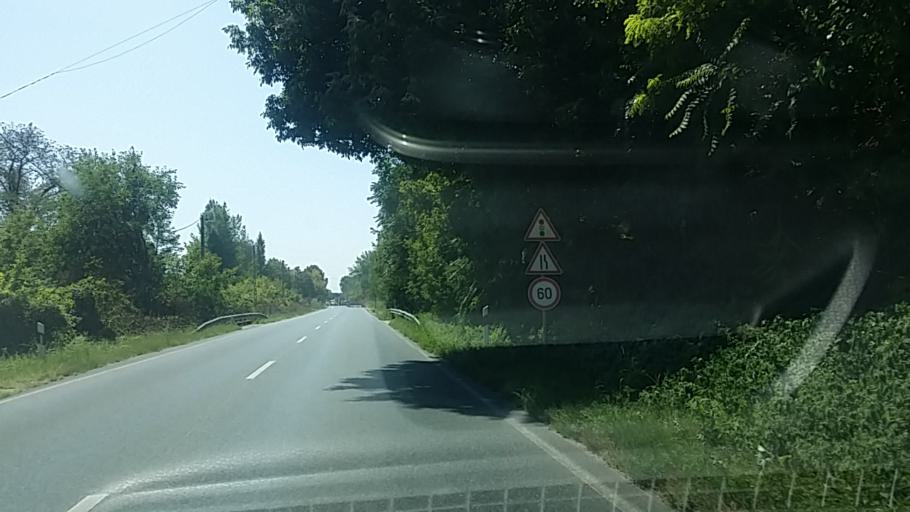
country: HU
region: Tolna
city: Paks
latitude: 46.6435
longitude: 18.8793
